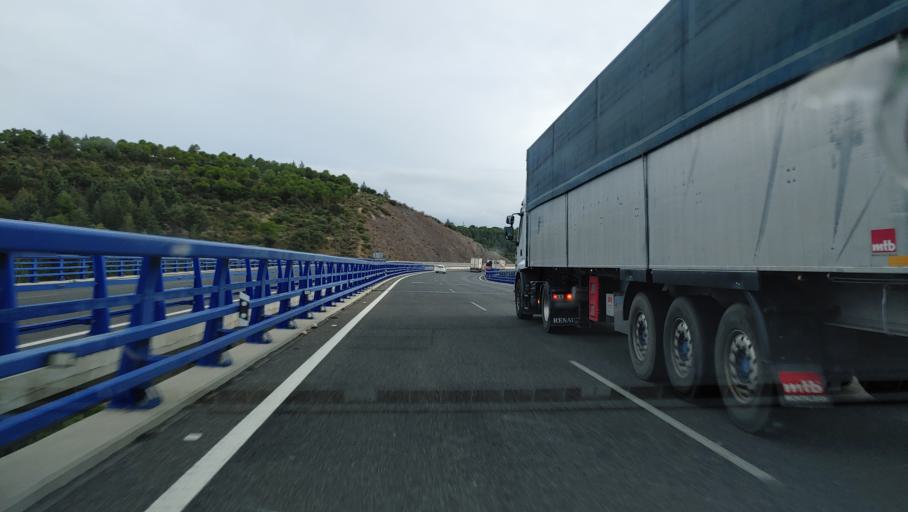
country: ES
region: Andalusia
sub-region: Provincia de Jaen
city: Santa Elena
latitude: 38.3545
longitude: -3.5293
